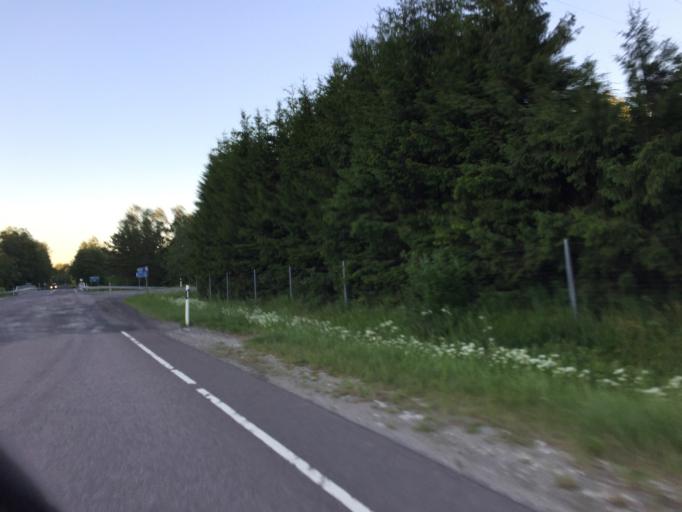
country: EE
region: Harju
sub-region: Raasiku vald
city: Raasiku
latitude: 59.4413
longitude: 25.1880
